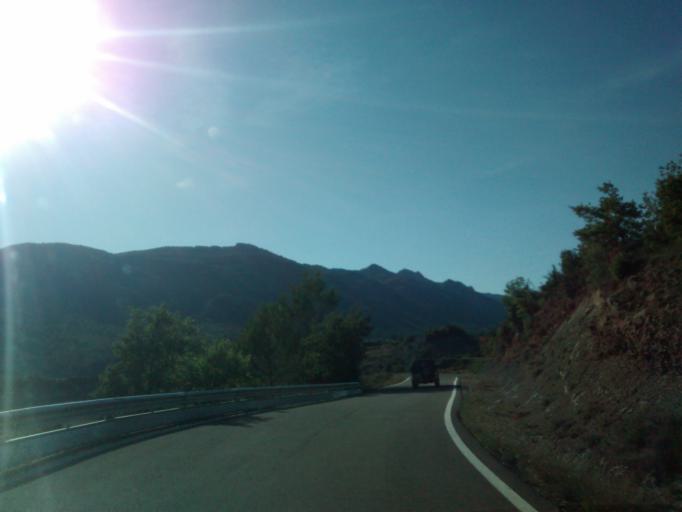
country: ES
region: Aragon
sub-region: Provincia de Zaragoza
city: Santa Eulalia de Gallego
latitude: 42.3943
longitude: -0.7345
